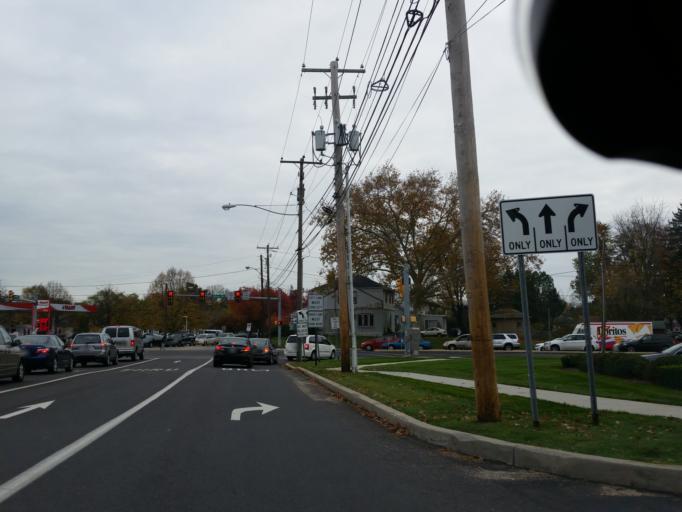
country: US
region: Pennsylvania
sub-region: Cumberland County
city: Camp Hill
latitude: 40.2382
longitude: -76.9350
